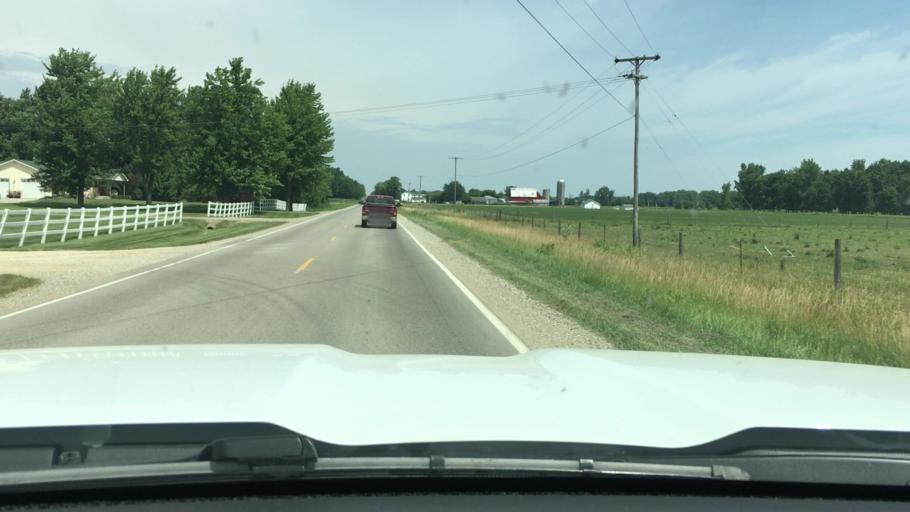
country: US
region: Michigan
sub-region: Sanilac County
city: Brown City
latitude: 43.2953
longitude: -82.9832
